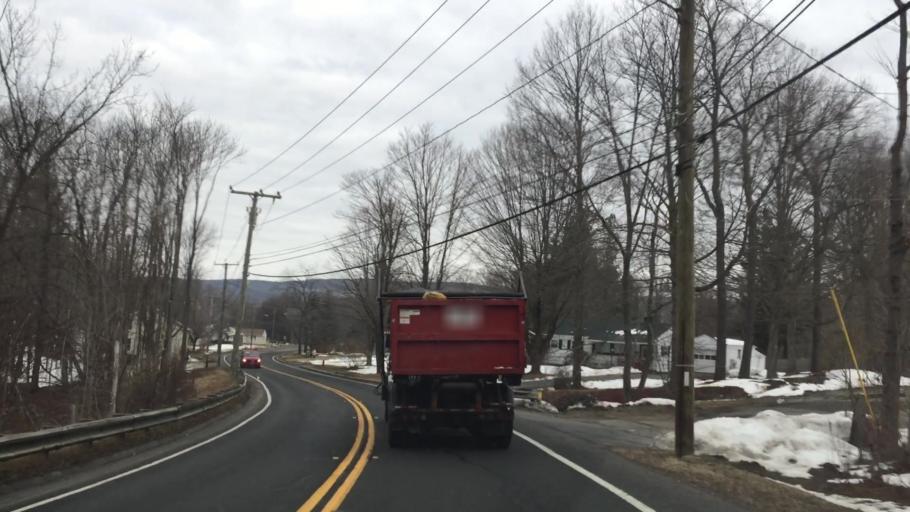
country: US
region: Massachusetts
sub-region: Berkshire County
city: Hinsdale
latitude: 42.4641
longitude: -73.1378
